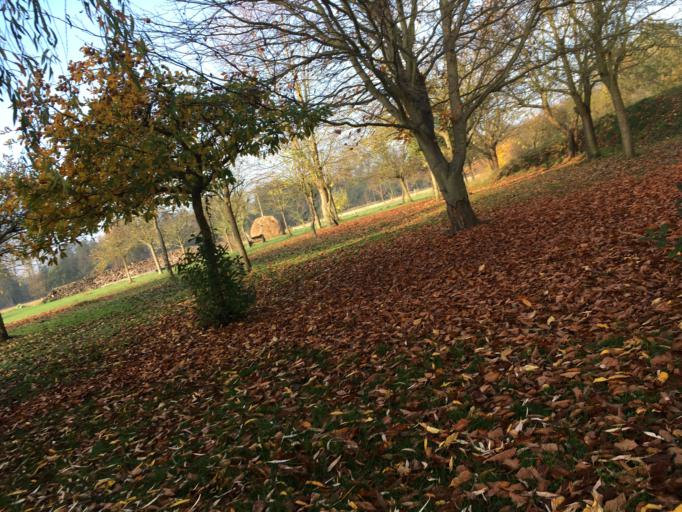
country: DE
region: Brandenburg
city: Schlepzig
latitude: 52.0305
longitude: 13.8894
